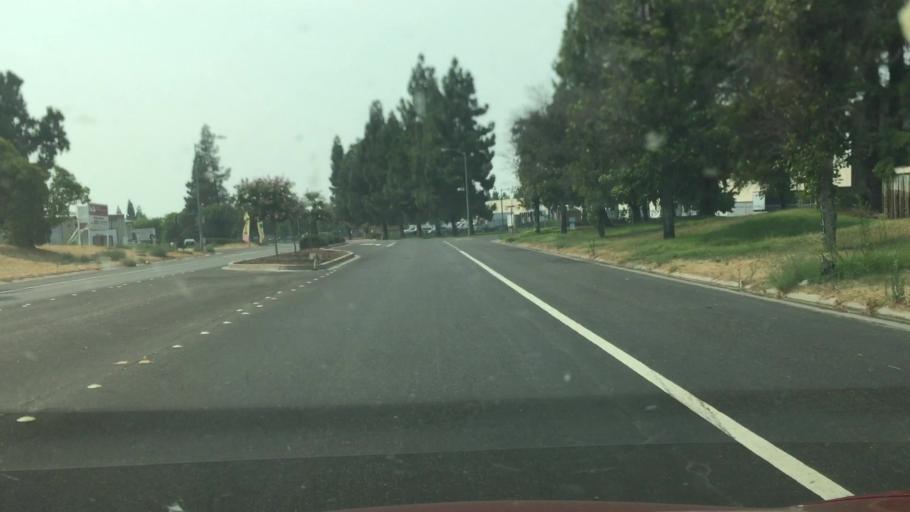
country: US
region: California
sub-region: San Joaquin County
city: Manteca
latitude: 37.7872
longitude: -121.2128
